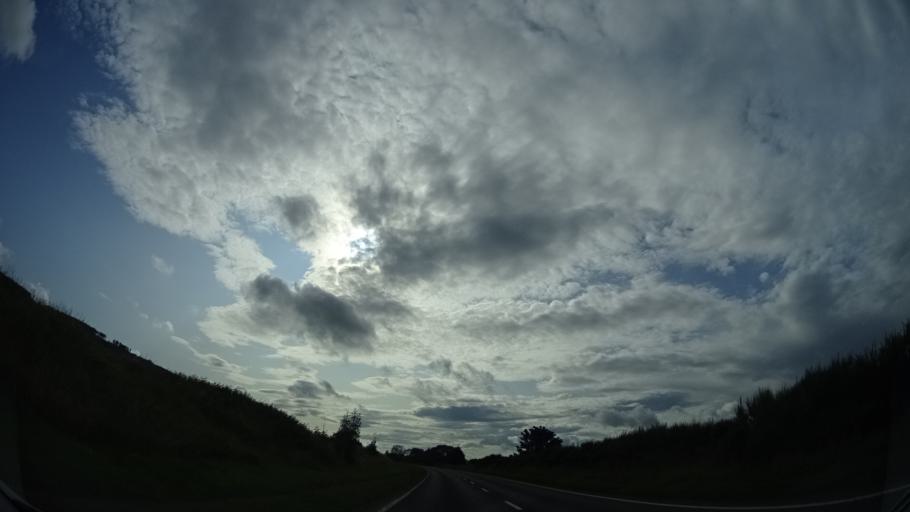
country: GB
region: Scotland
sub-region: Highland
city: Muir of Ord
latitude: 57.5591
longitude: -4.5479
